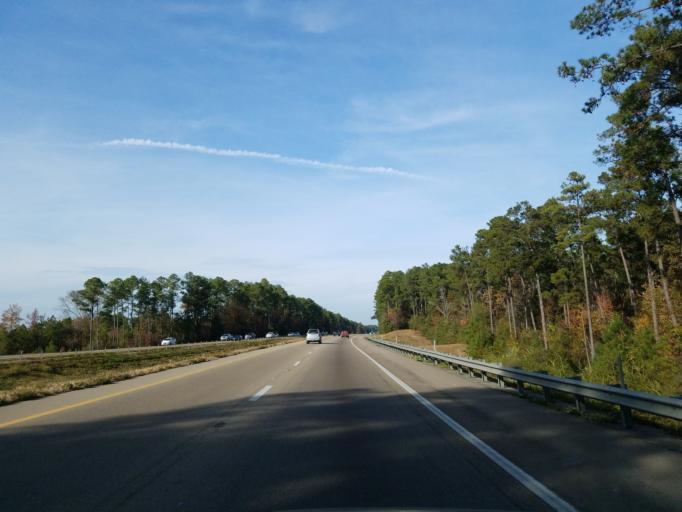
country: US
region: Mississippi
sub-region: Lamar County
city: West Hattiesburg
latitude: 31.2865
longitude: -89.3524
